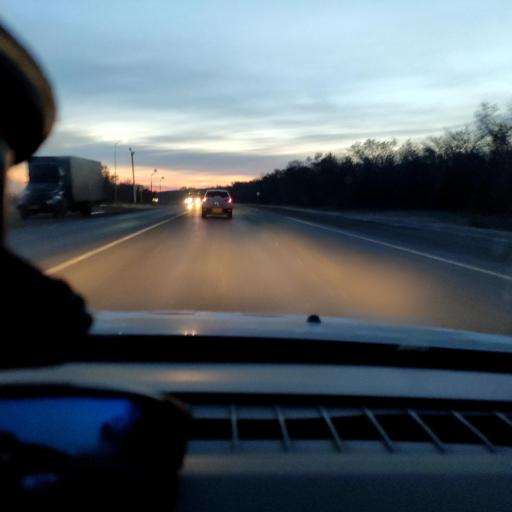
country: RU
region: Samara
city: Samara
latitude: 53.0811
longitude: 50.1229
